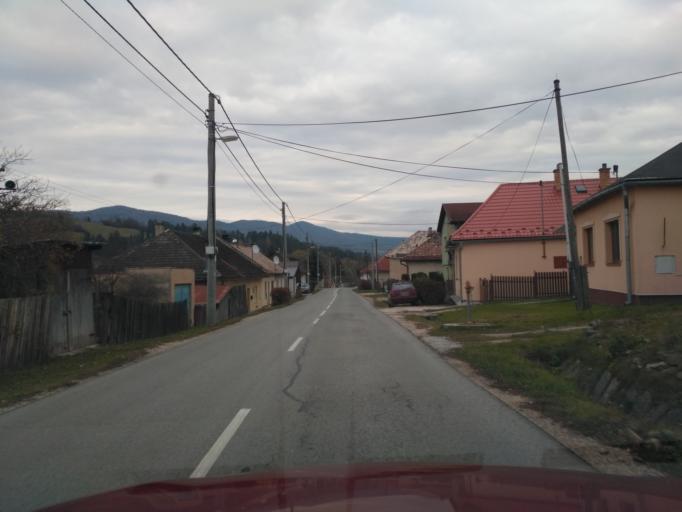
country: SK
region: Kosicky
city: Krompachy
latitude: 48.8031
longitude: 20.7974
